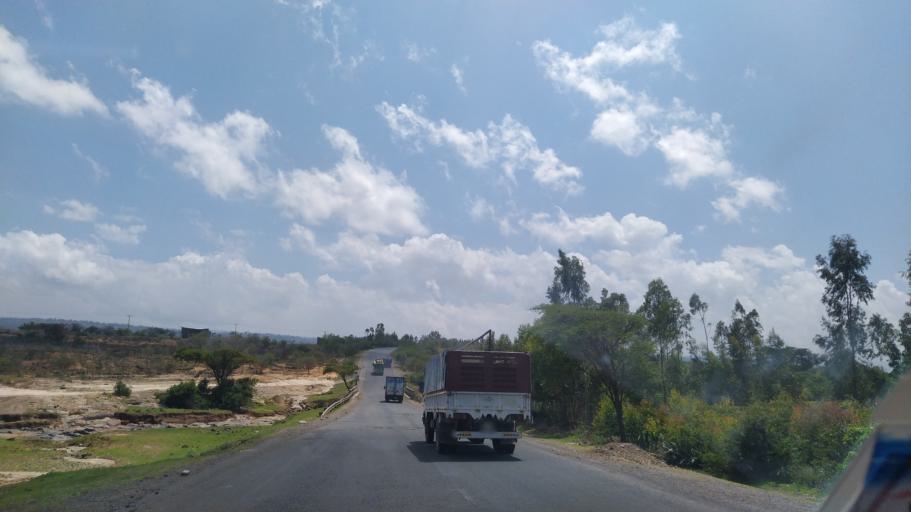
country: ET
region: Southern Nations, Nationalities, and People's Region
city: Butajira
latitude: 7.7744
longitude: 38.1394
